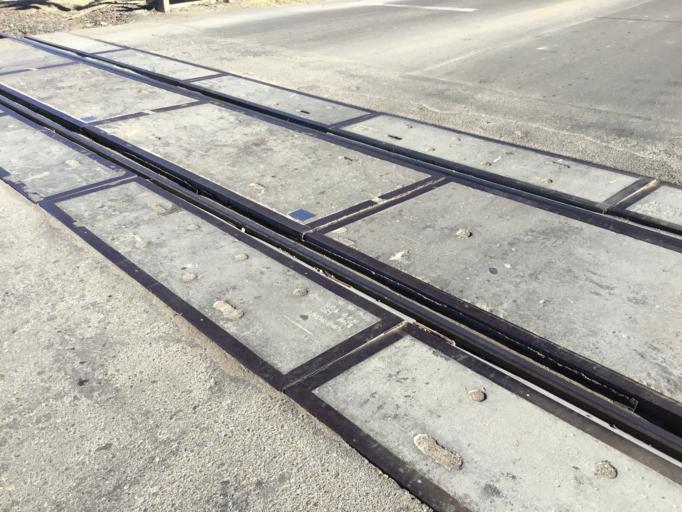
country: US
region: Kansas
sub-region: Geary County
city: Junction City
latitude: 39.0303
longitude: -96.8242
